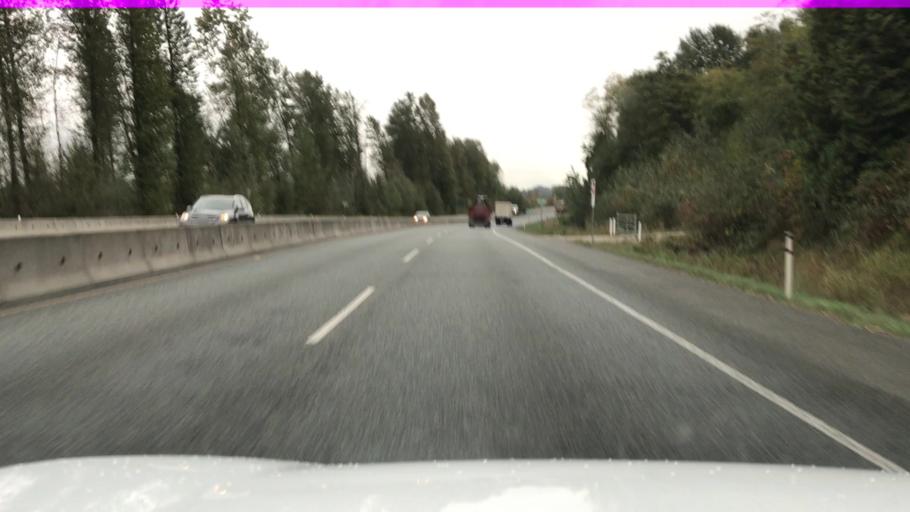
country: CA
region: British Columbia
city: Coquitlam
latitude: 49.2119
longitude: -122.7903
